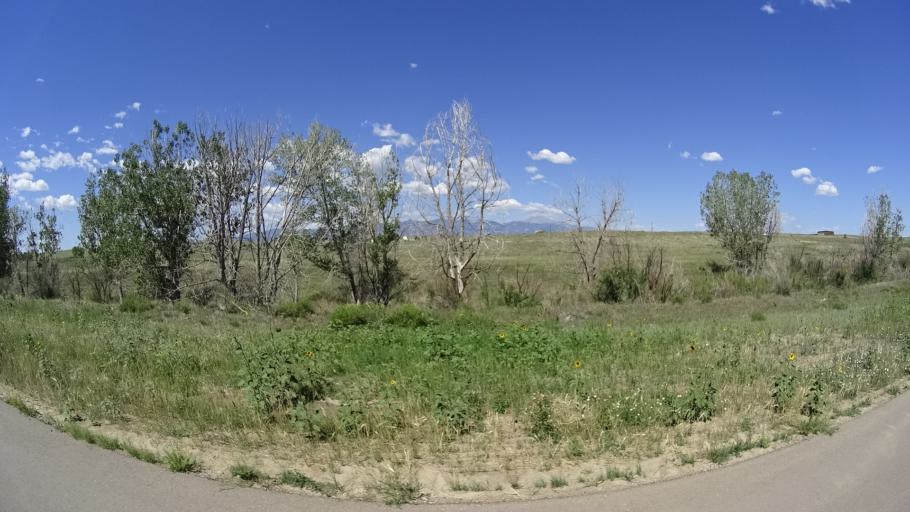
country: US
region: Colorado
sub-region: El Paso County
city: Security-Widefield
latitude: 38.7649
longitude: -104.6598
